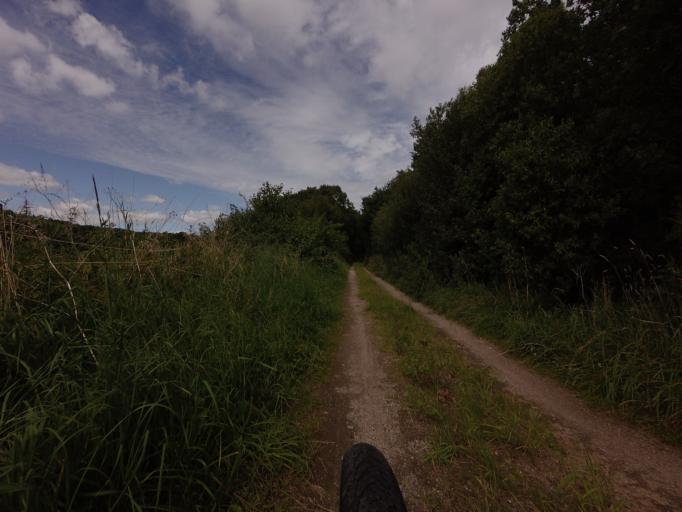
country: DK
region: Central Jutland
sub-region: Syddjurs Kommune
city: Ryomgard
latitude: 56.3953
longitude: 10.5316
